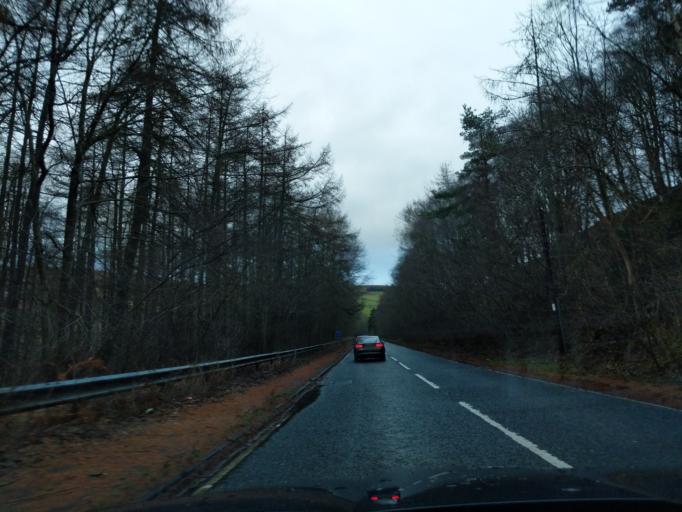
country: GB
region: Scotland
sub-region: The Scottish Borders
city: Galashiels
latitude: 55.6332
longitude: -2.8296
